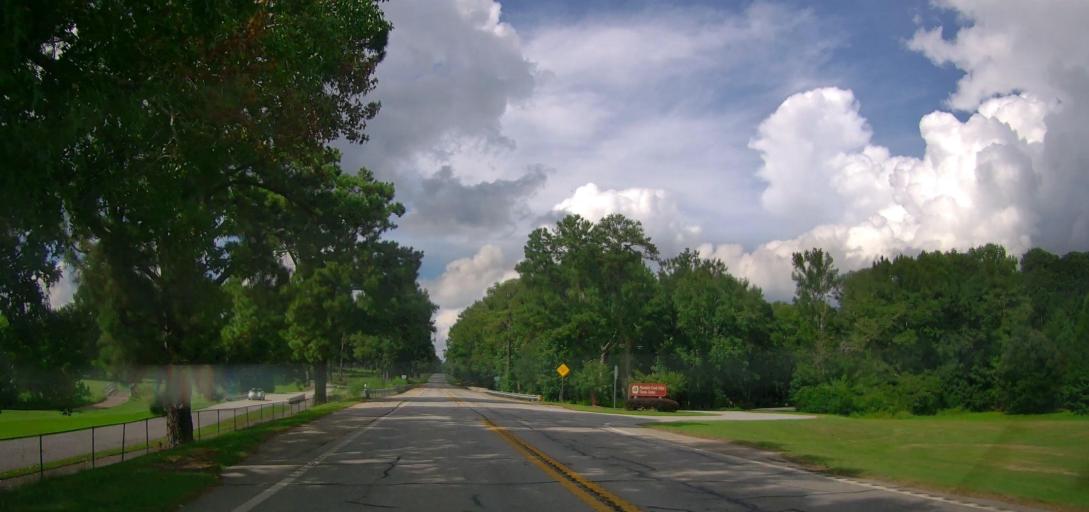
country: US
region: Georgia
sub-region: Harris County
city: Pine Mountain
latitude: 32.8314
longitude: -84.8437
